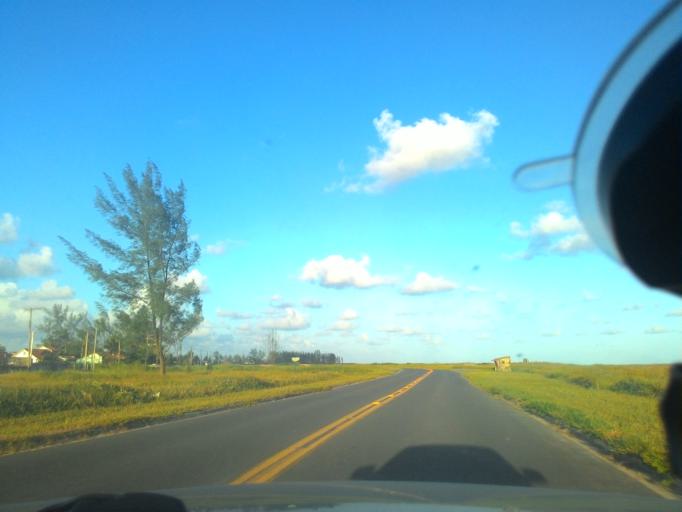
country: BR
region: Sao Paulo
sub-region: Iguape
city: Iguape
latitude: -24.8039
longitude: -47.6347
